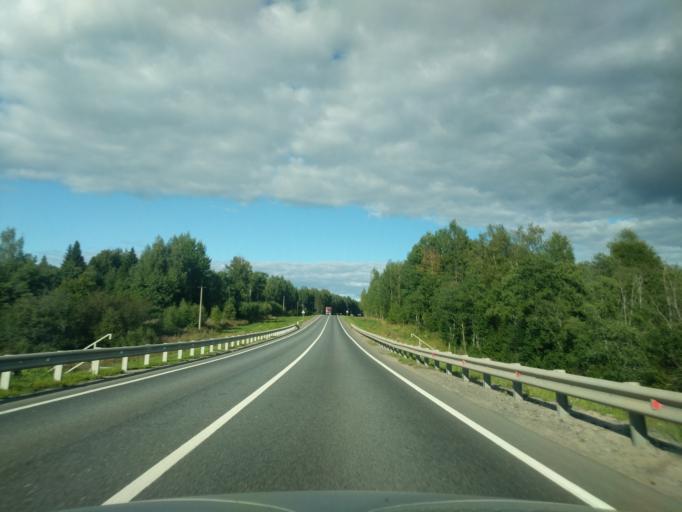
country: RU
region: Kostroma
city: Manturovo
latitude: 58.1628
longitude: 44.3990
